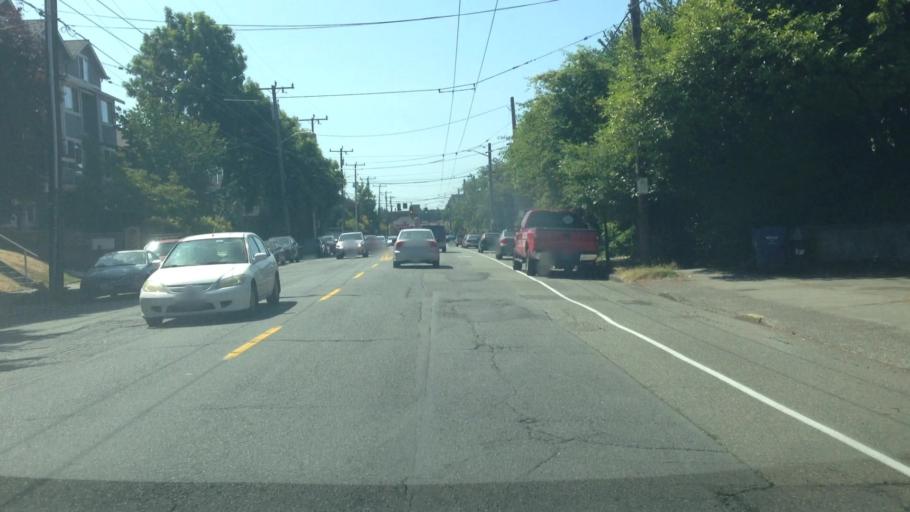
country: US
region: Washington
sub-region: King County
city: Seattle
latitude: 47.6281
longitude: -122.3203
